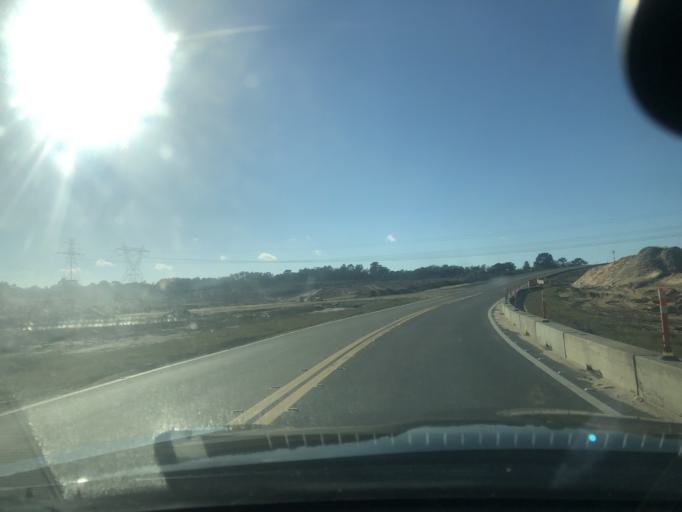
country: US
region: Florida
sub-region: Citrus County
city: Sugarmill Woods
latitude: 28.7635
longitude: -82.4978
